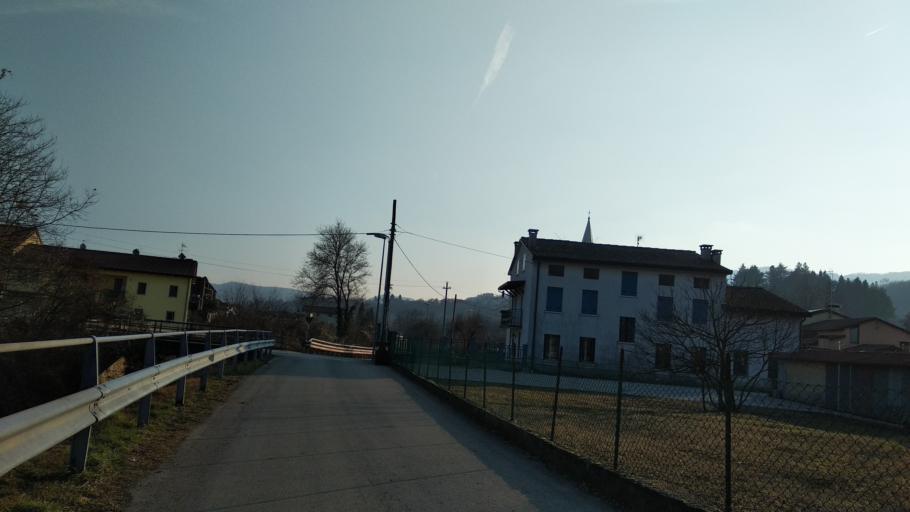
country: IT
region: Veneto
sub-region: Provincia di Vicenza
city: San Vito di Leguzzano
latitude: 45.6839
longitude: 11.3737
